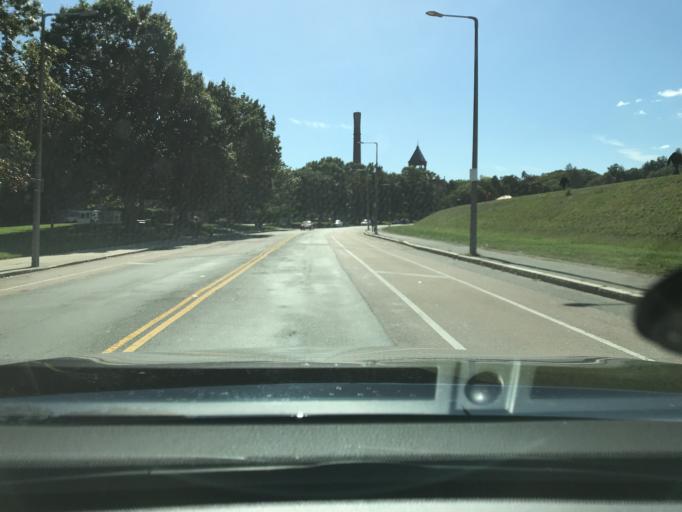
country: US
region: Massachusetts
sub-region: Norfolk County
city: Brookline
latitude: 42.3340
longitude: -71.1541
